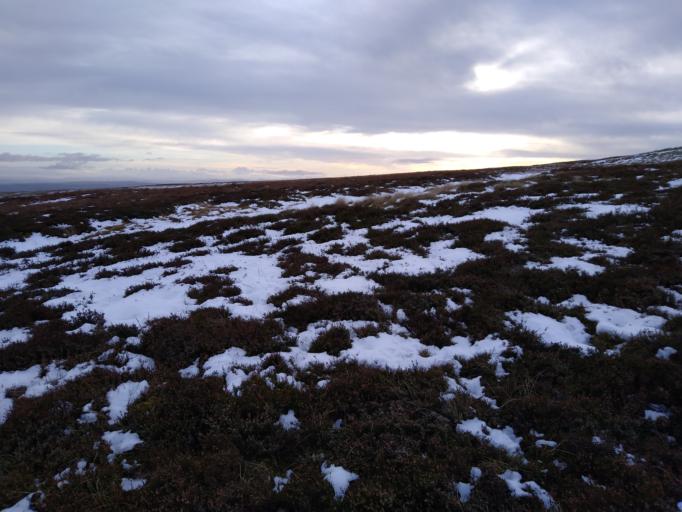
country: GB
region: England
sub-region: Cumbria
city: Penrith
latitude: 54.5791
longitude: -2.8324
